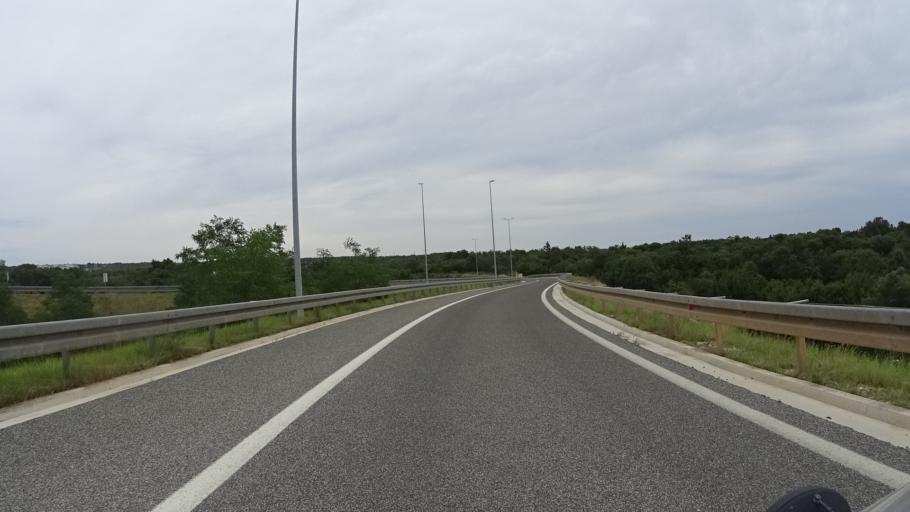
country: HR
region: Istarska
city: Vodnjan
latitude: 45.1110
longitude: 13.8111
